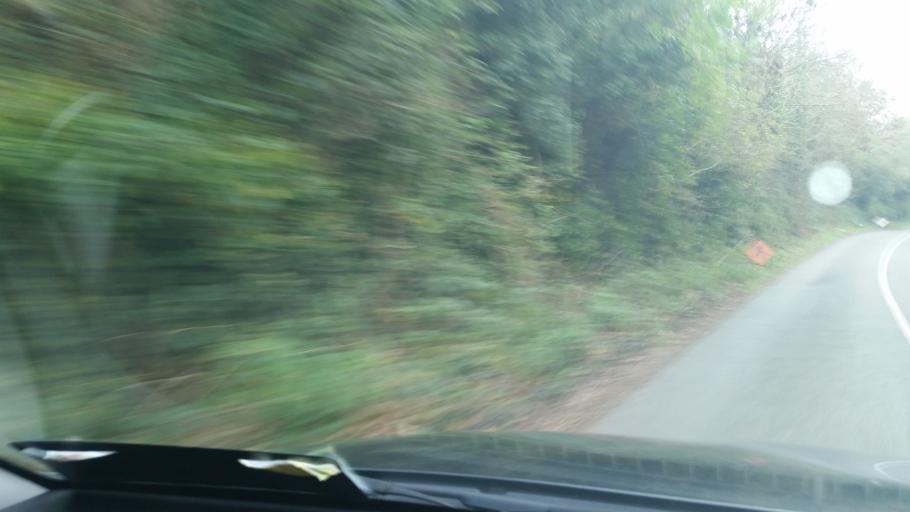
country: IE
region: Leinster
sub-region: An Mhi
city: Duleek
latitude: 53.6952
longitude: -6.4307
